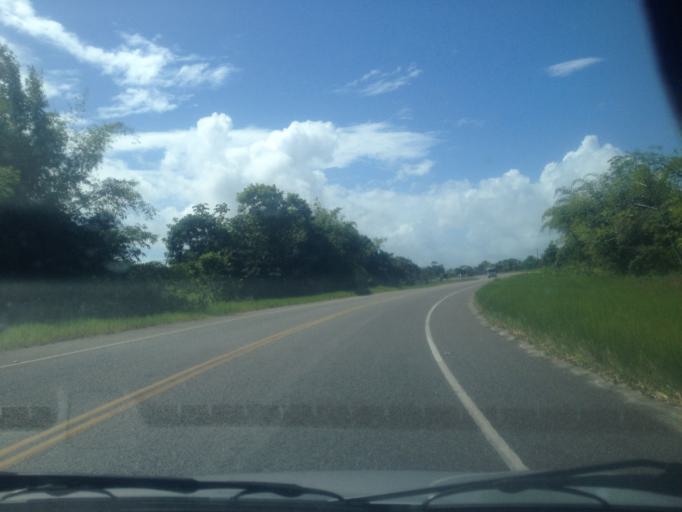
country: BR
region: Bahia
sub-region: Conde
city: Conde
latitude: -11.7597
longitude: -37.5902
